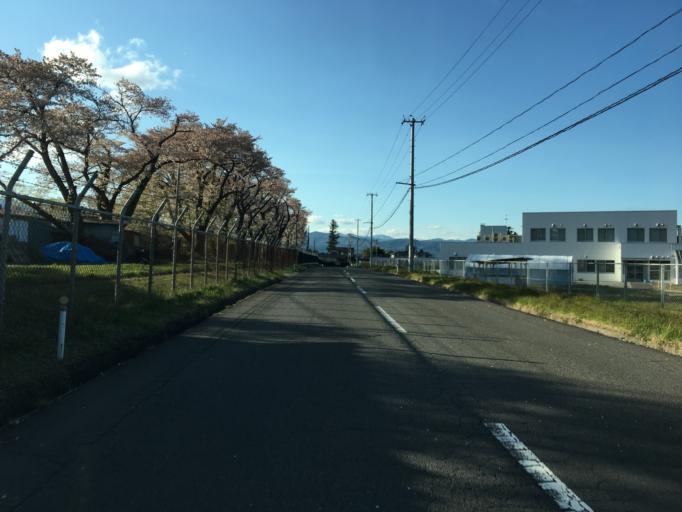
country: JP
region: Fukushima
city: Fukushima-shi
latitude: 37.7127
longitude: 140.3859
